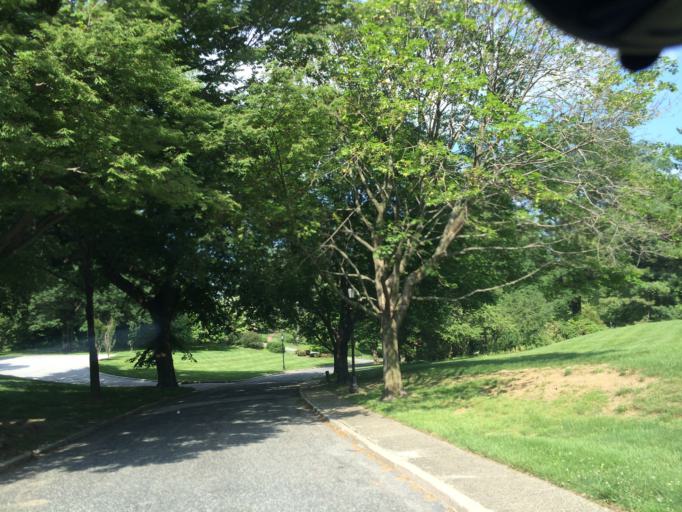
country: US
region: Maryland
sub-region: Baltimore County
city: Towson
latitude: 39.3603
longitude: -76.6252
